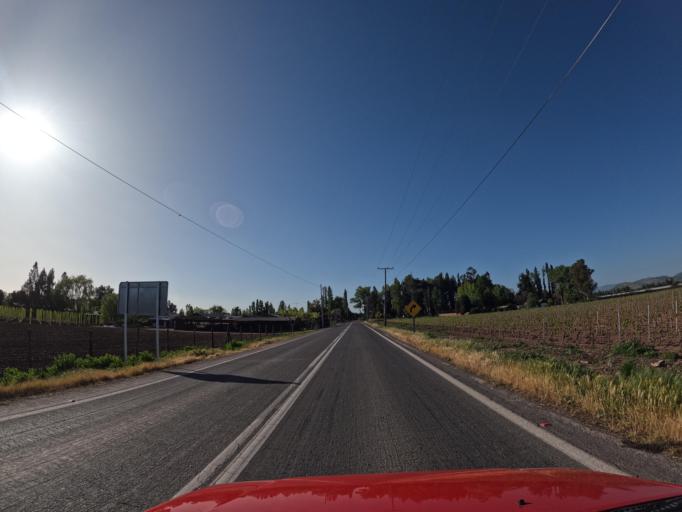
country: CL
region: Maule
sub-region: Provincia de Curico
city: Teno
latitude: -34.7572
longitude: -71.2397
